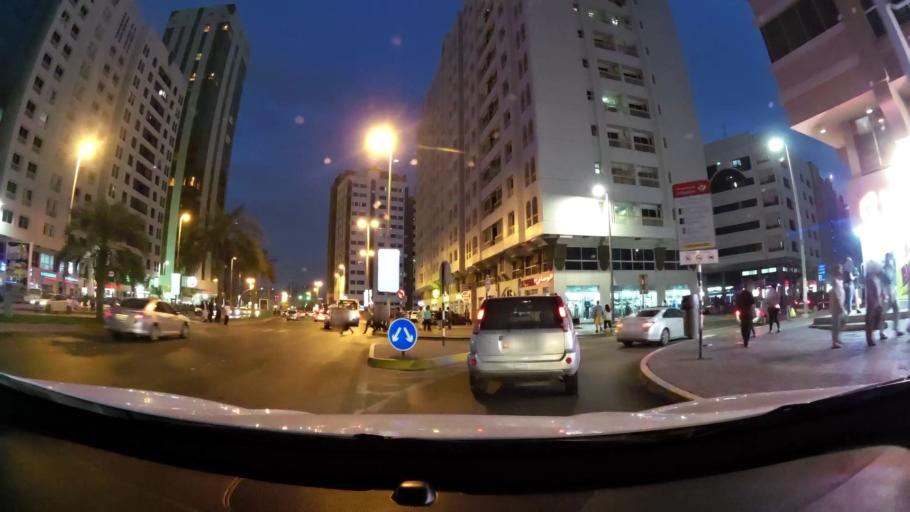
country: AE
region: Abu Dhabi
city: Abu Dhabi
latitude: 24.4886
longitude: 54.3639
